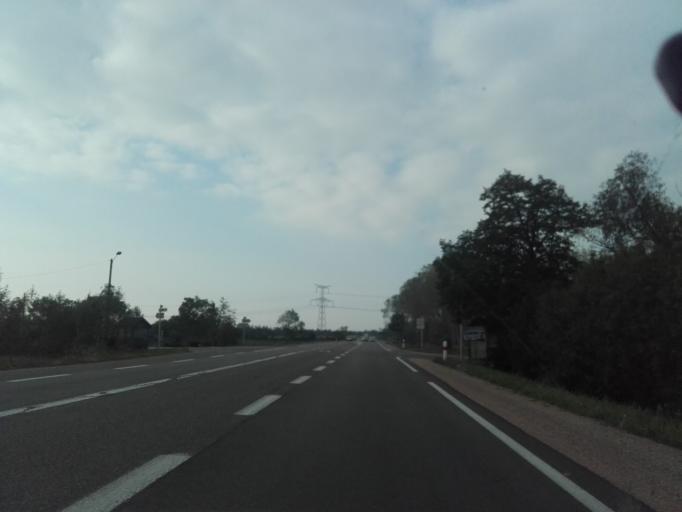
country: FR
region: Bourgogne
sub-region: Departement de Saone-et-Loire
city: La Chapelle-de-Guinchay
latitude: 46.1986
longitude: 4.7640
